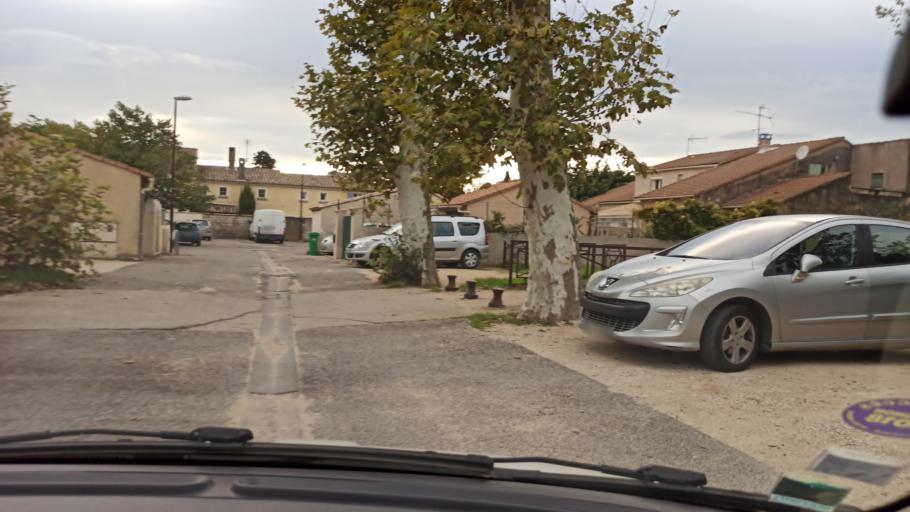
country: FR
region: Provence-Alpes-Cote d'Azur
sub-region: Departement du Vaucluse
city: Montfavet
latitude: 43.9304
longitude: 4.8788
